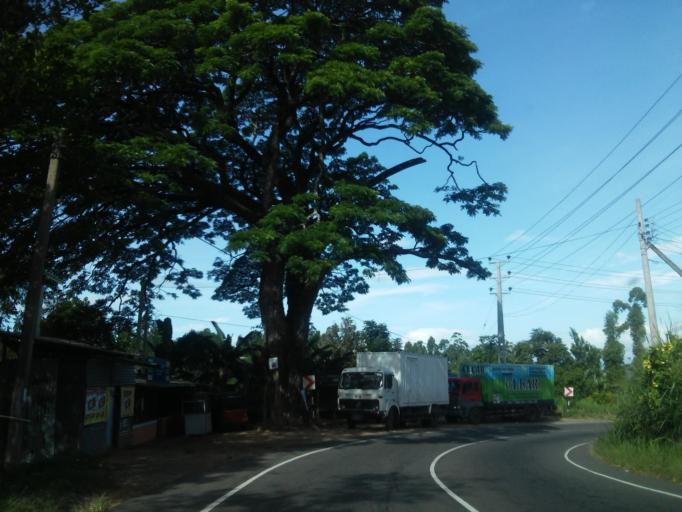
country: LK
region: Uva
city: Haputale
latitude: 6.7610
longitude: 80.8767
